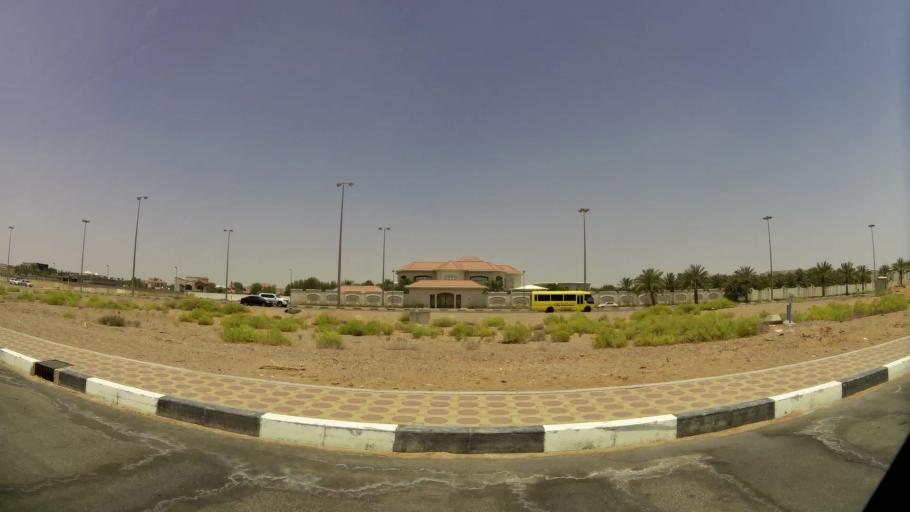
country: OM
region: Al Buraimi
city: Al Buraymi
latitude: 24.2642
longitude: 55.7197
